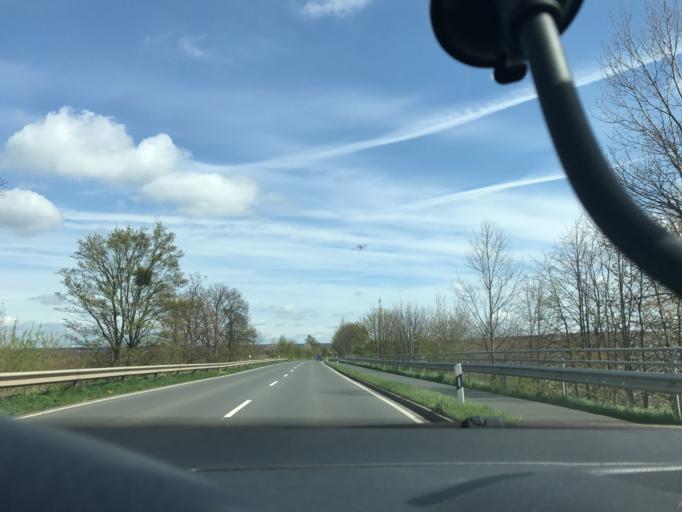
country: DE
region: Lower Saxony
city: Helmstedt
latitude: 52.2070
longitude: 10.9821
